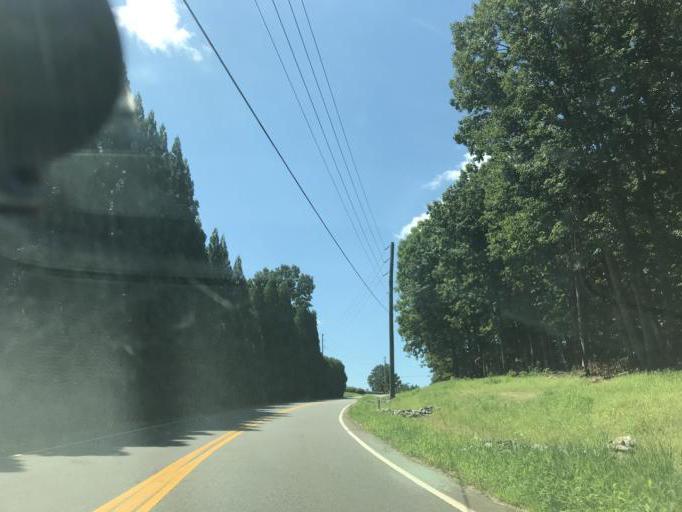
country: US
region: Georgia
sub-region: Dawson County
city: Dawsonville
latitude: 34.3067
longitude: -84.0289
